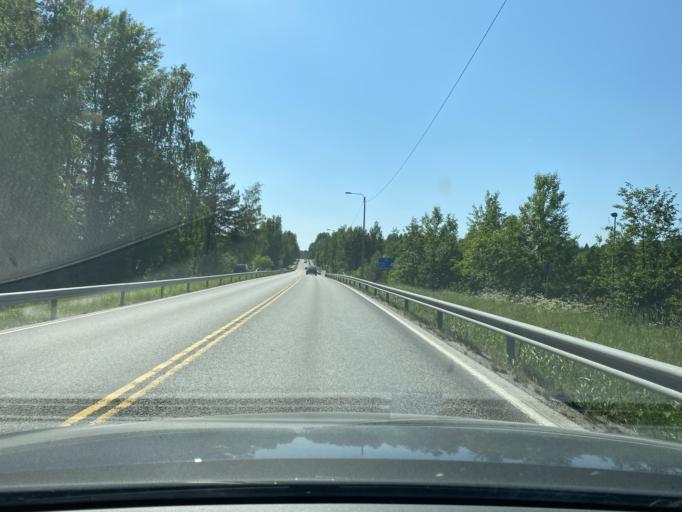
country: FI
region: Pirkanmaa
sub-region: Tampere
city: Nokia
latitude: 61.4796
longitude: 23.5448
